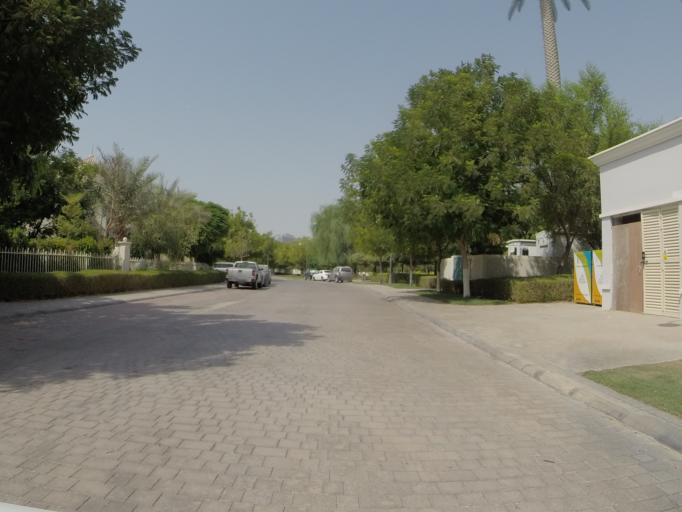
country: AE
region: Dubai
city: Dubai
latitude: 25.0340
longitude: 55.2141
